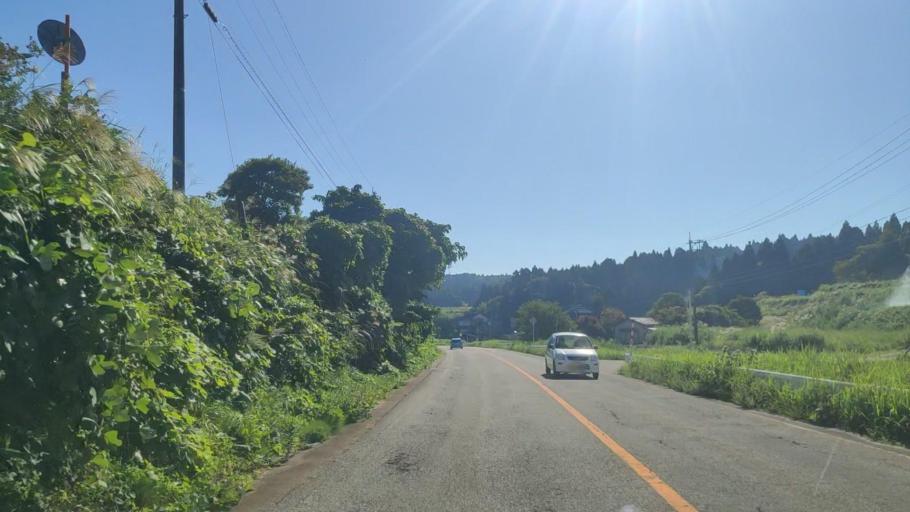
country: JP
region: Ishikawa
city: Nanao
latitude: 37.2658
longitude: 137.0918
